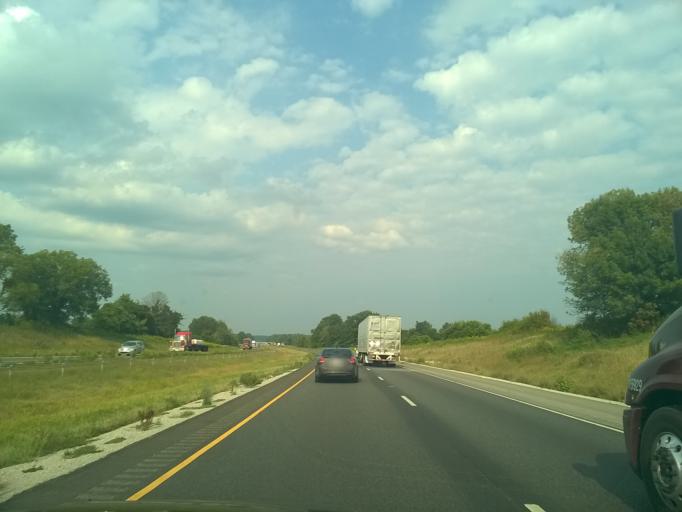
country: US
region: Indiana
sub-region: Clay County
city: Brazil
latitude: 39.4712
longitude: -87.0273
